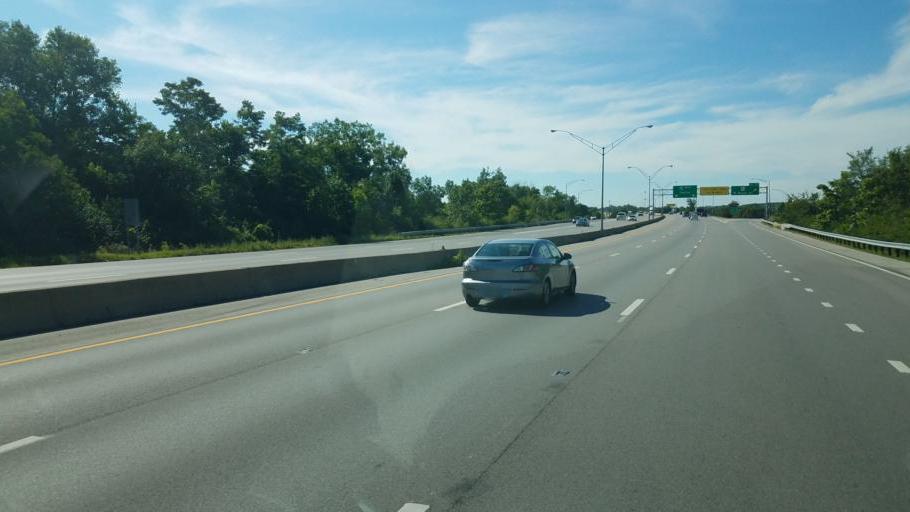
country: US
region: Ohio
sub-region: Franklin County
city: Grandview Heights
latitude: 39.9527
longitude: -83.0410
